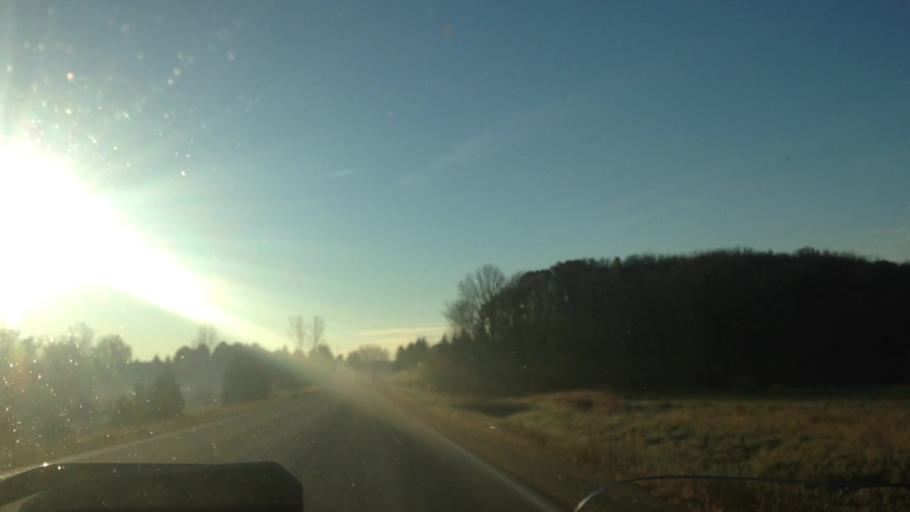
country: US
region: Wisconsin
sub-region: Dodge County
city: Mayville
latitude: 43.4826
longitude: -88.5096
